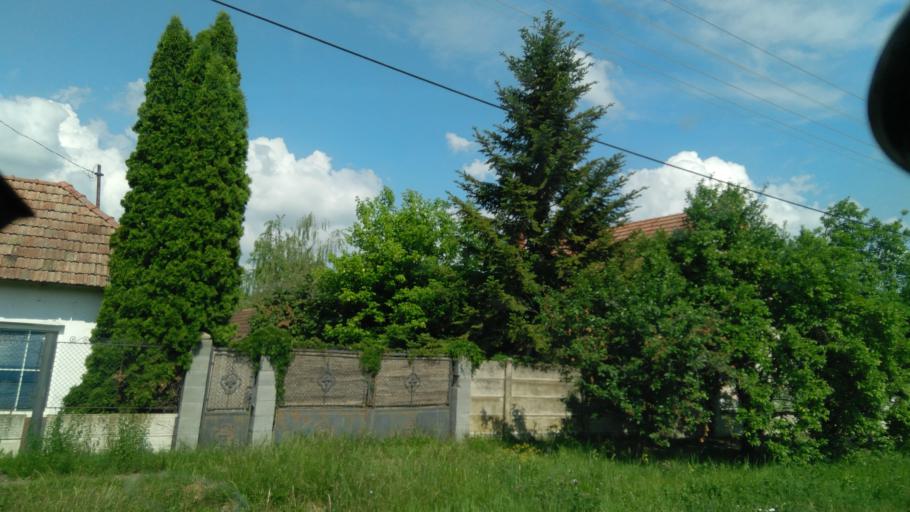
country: HU
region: Bekes
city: Doboz
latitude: 46.7397
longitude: 21.2339
